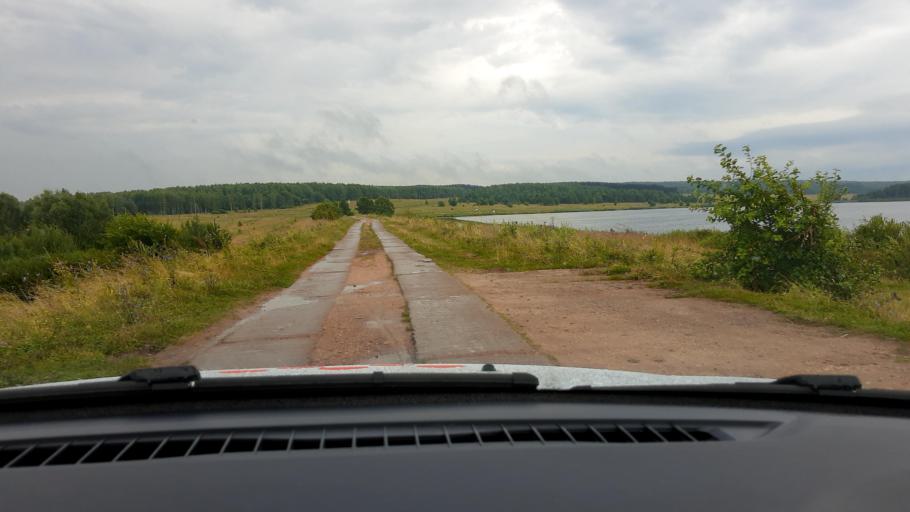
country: RU
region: Nizjnij Novgorod
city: Surovatikha
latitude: 55.9365
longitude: 43.9170
